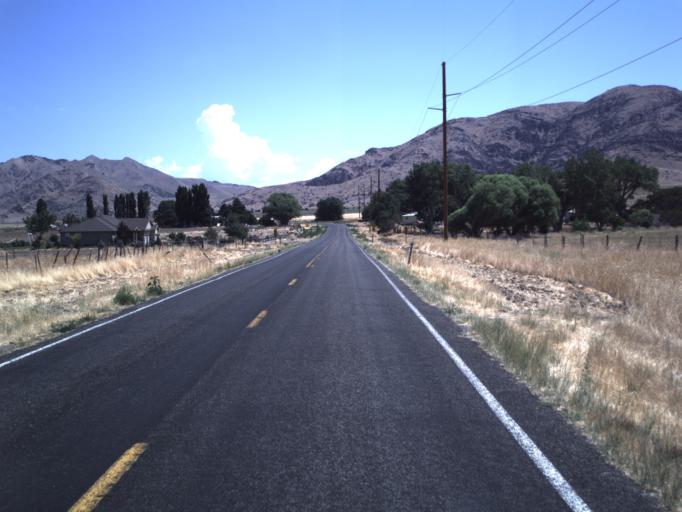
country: US
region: Utah
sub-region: Millard County
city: Delta
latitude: 39.4692
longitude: -112.2738
